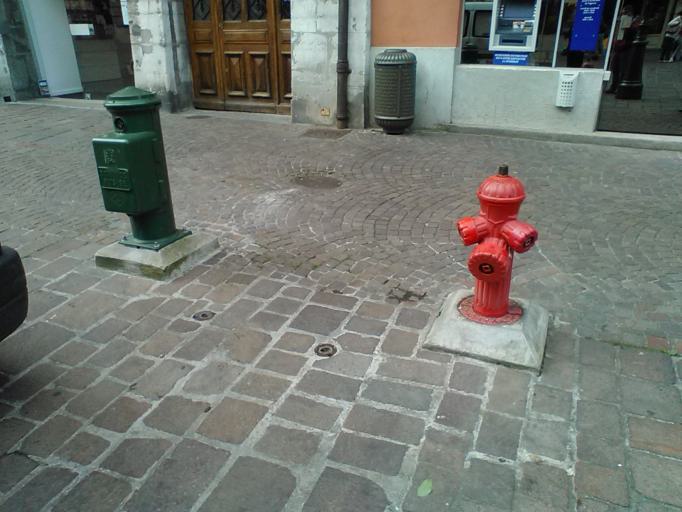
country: FR
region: Rhone-Alpes
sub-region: Departement de la Savoie
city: Chambery
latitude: 45.5646
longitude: 5.9211
